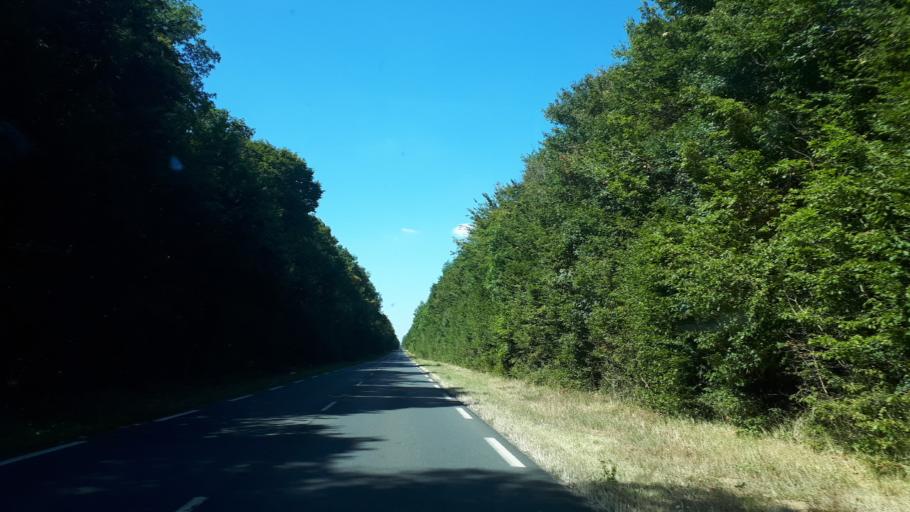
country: FR
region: Centre
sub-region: Departement du Loir-et-Cher
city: Mont-pres-Chambord
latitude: 47.5622
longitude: 1.4193
